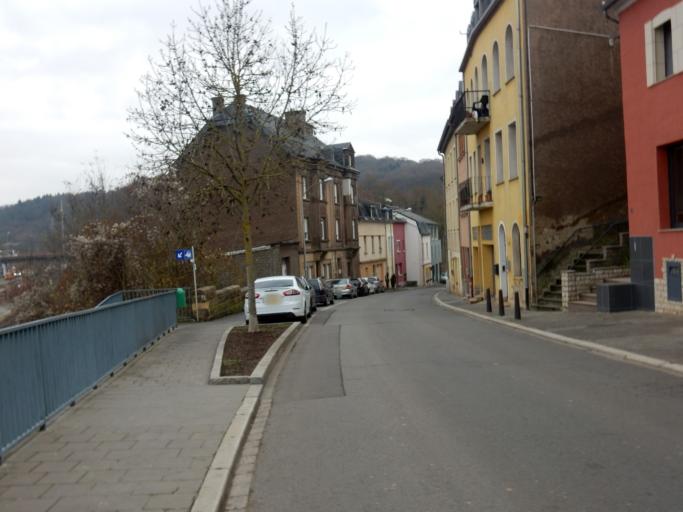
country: LU
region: Luxembourg
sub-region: Canton d'Esch-sur-Alzette
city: Dudelange
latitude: 49.4739
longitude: 6.0798
